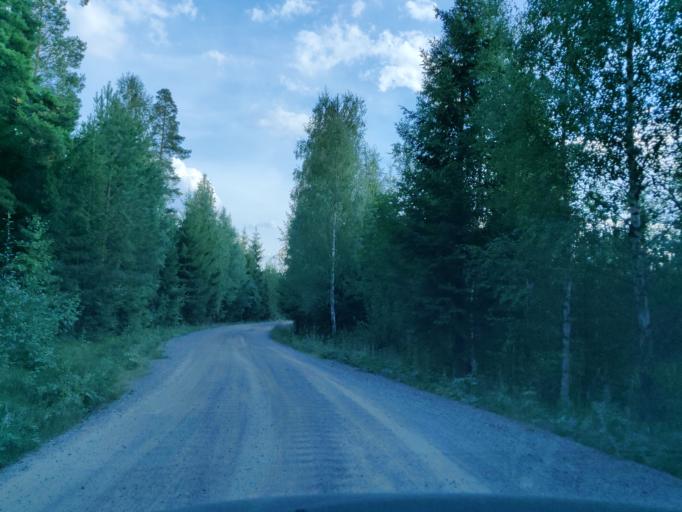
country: SE
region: Vaermland
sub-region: Hagfors Kommun
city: Hagfors
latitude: 60.0173
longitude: 13.6755
